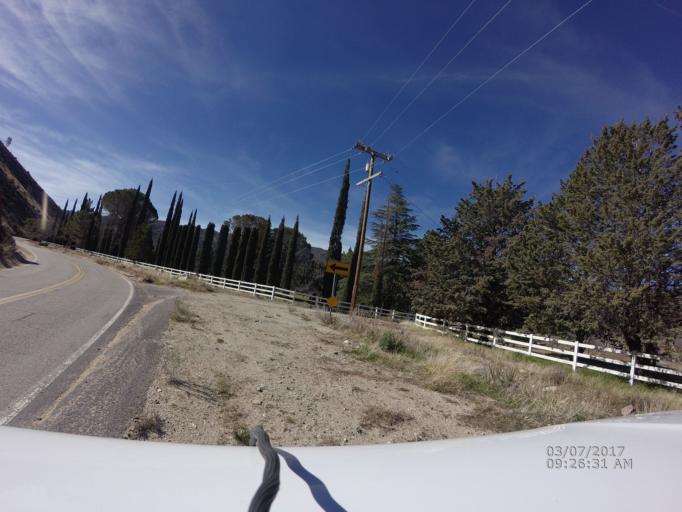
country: US
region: California
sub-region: Los Angeles County
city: Green Valley
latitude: 34.7417
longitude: -118.6002
